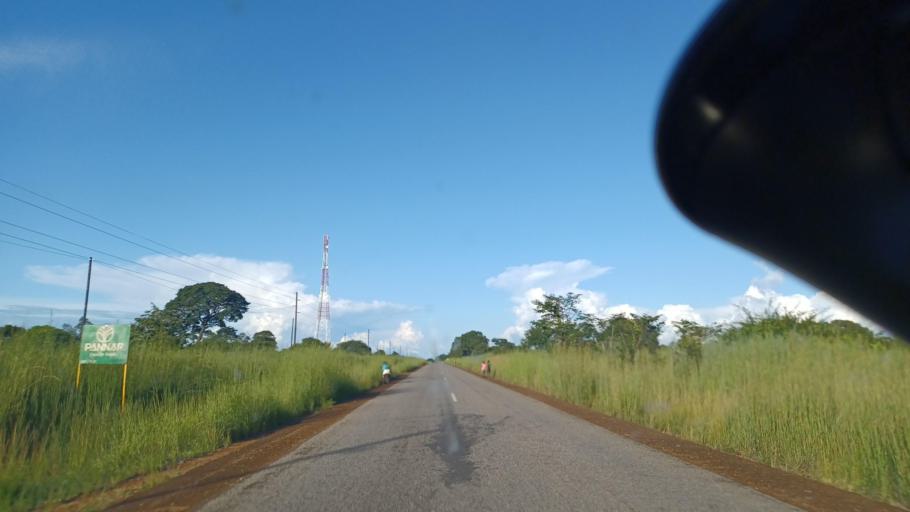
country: ZM
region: North-Western
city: Kalengwa
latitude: -13.1897
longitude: 24.8387
